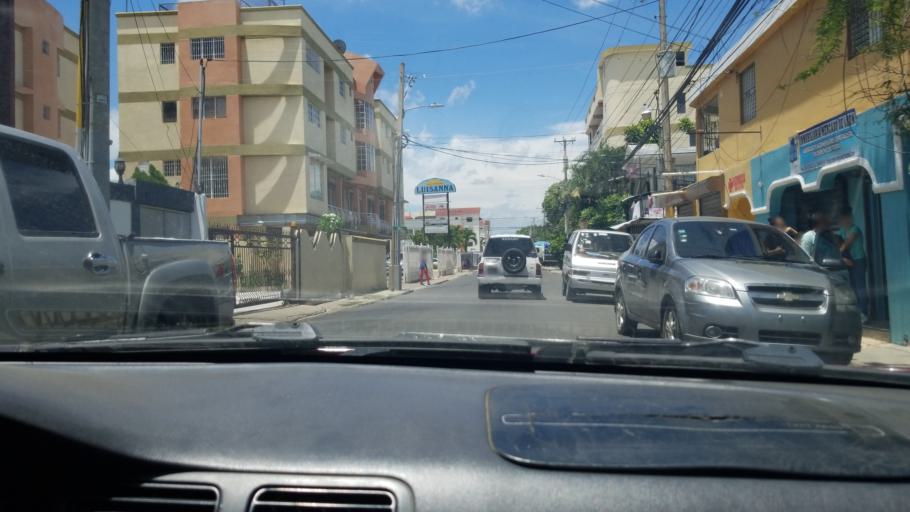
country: DO
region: Santiago
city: Santiago de los Caballeros
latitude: 19.4764
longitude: -70.6896
